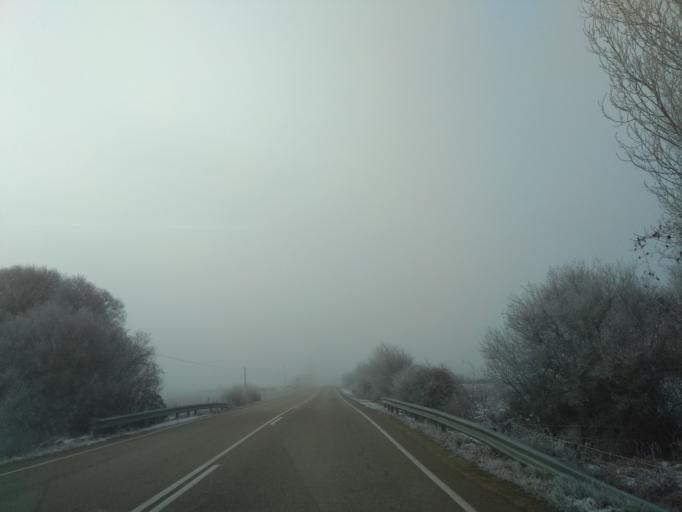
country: ES
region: Castille and Leon
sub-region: Provincia de Burgos
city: Espinosa de los Monteros
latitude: 43.0358
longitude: -3.4968
